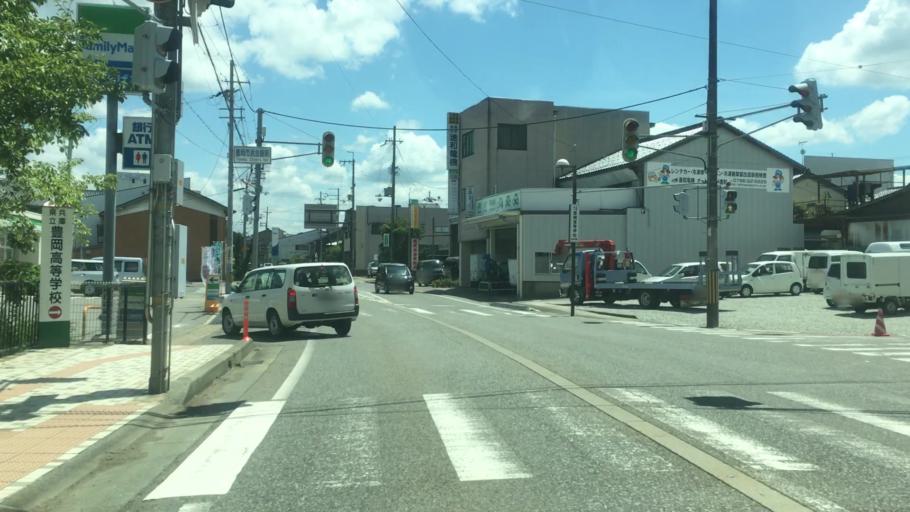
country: JP
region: Hyogo
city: Toyooka
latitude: 35.5403
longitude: 134.8241
